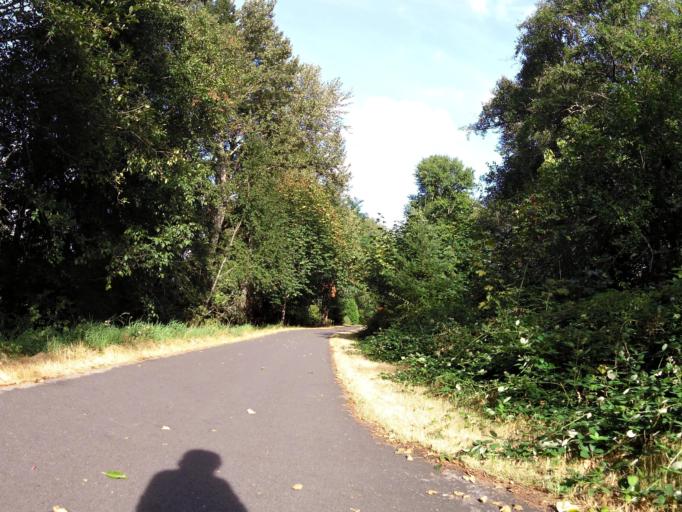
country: US
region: Washington
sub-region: Thurston County
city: Lacey
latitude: 47.0401
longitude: -122.8519
